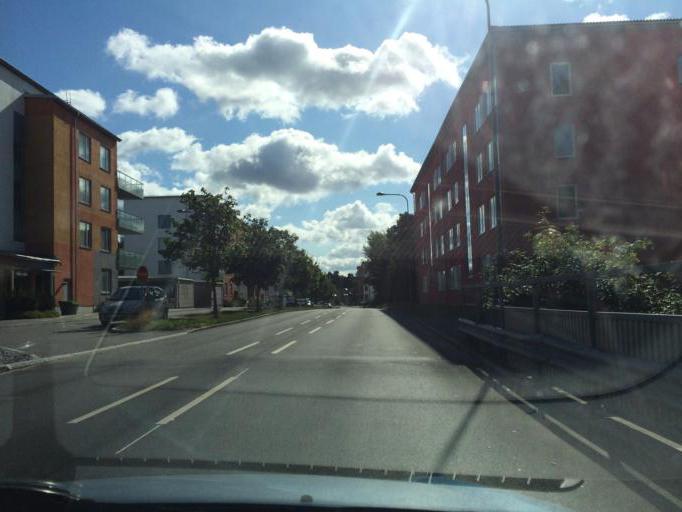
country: SE
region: Stockholm
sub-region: Nacka Kommun
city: Nacka
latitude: 59.2818
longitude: 18.1238
